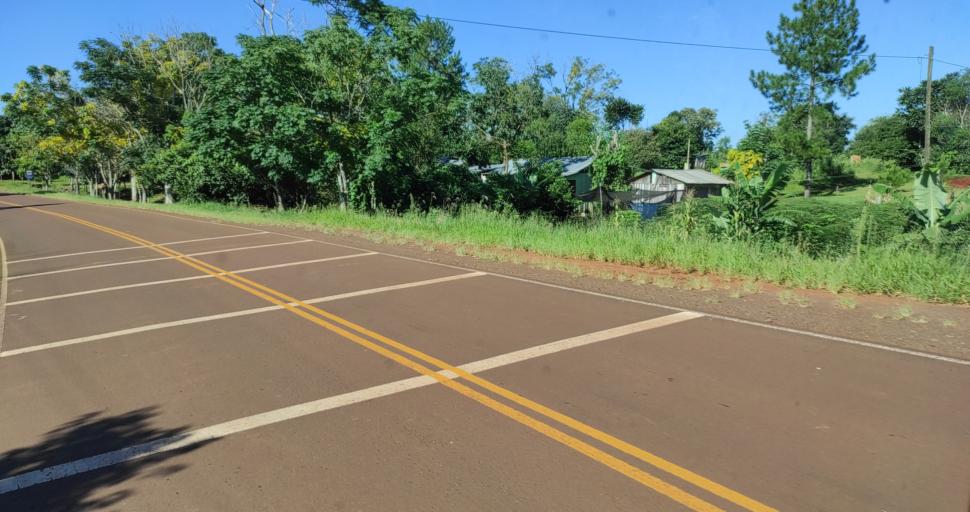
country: AR
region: Misiones
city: El Soberbio
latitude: -27.2292
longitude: -54.1783
